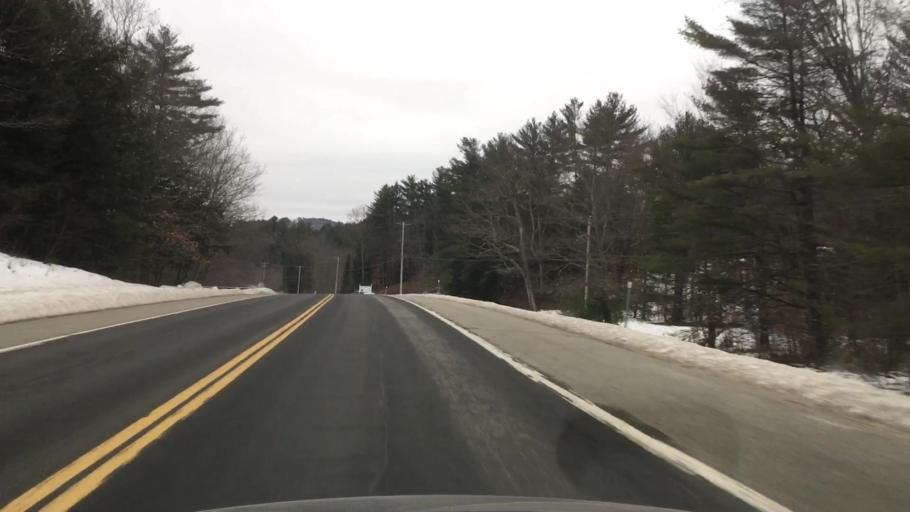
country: US
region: New Hampshire
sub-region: Merrimack County
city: Sutton
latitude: 43.2520
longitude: -71.9265
